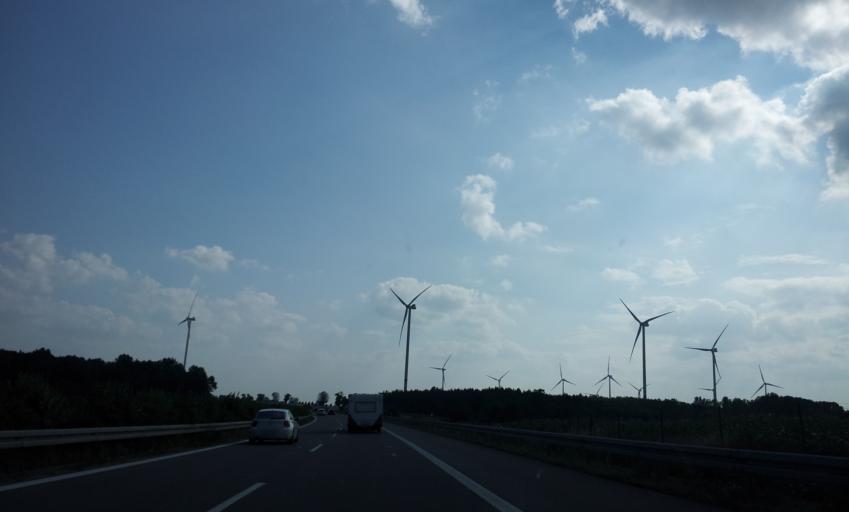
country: DE
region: Mecklenburg-Vorpommern
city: Jarmen
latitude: 53.9004
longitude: 13.3448
